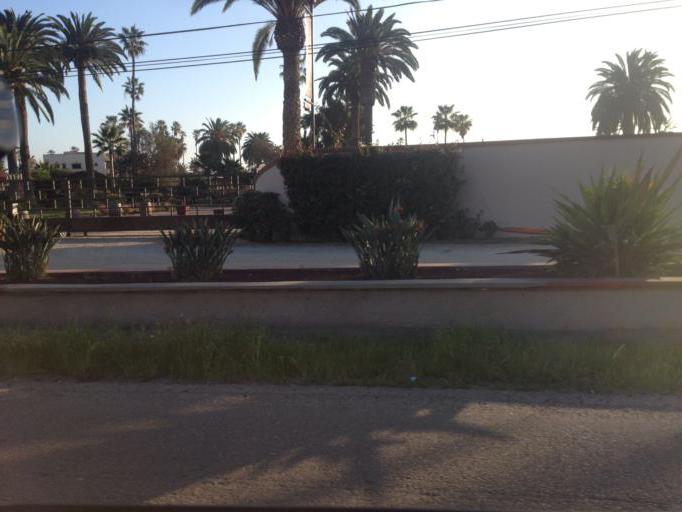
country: MX
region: Baja California
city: El Sauzal
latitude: 31.8644
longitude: -116.6571
